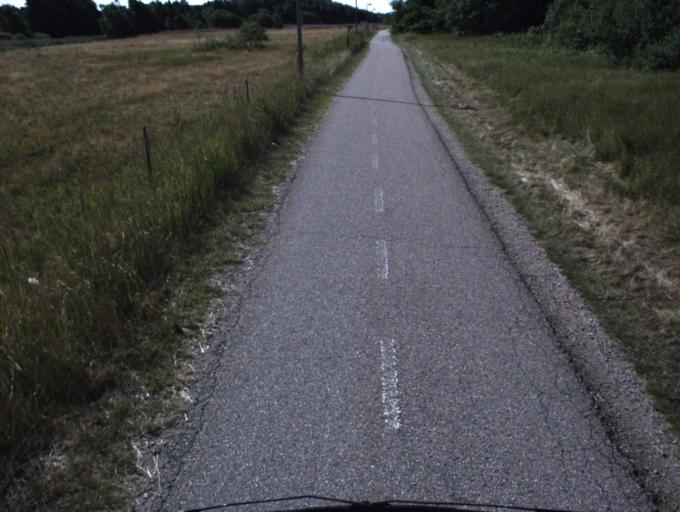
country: SE
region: Skane
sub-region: Helsingborg
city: Rydeback
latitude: 55.9854
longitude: 12.7534
